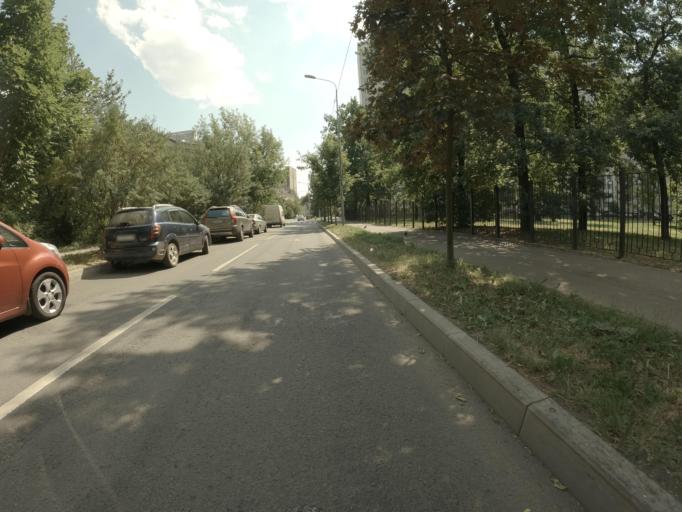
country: RU
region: St.-Petersburg
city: Avtovo
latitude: 59.8940
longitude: 30.2607
